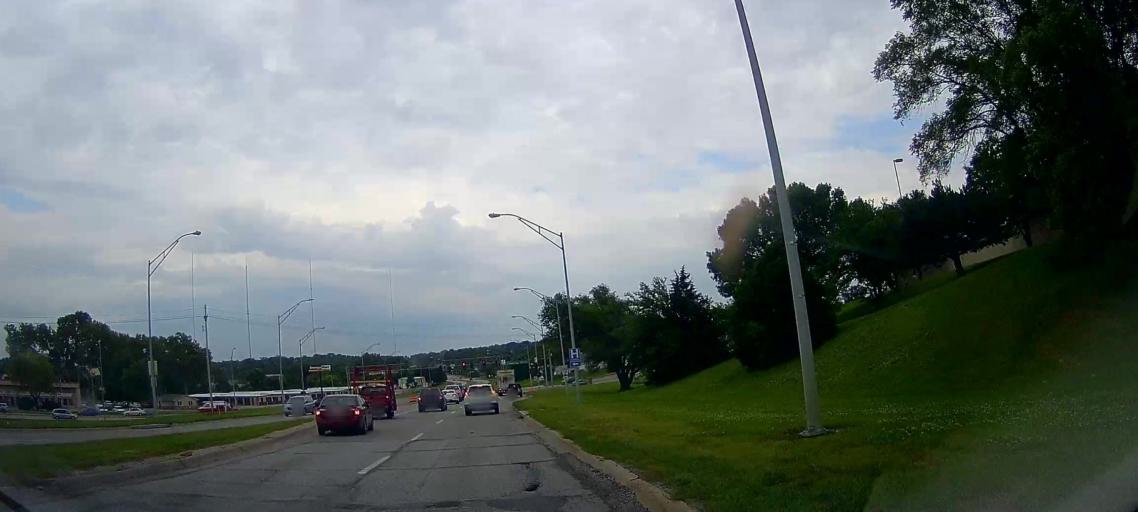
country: US
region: Nebraska
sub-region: Douglas County
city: Ralston
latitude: 41.3136
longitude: -96.0538
